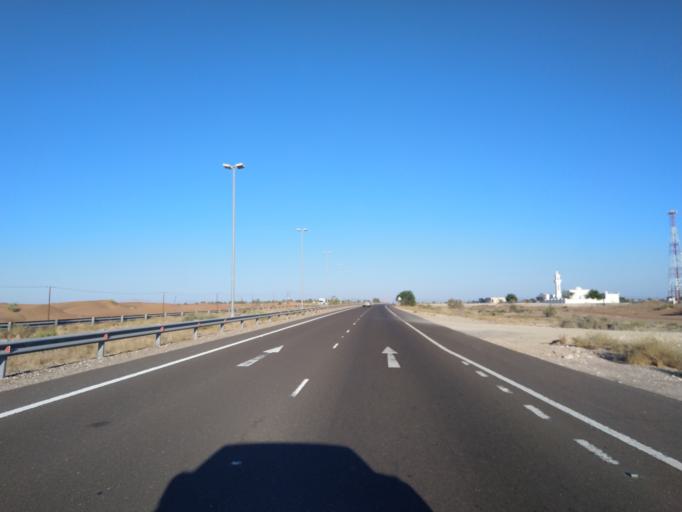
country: OM
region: Al Buraimi
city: Al Buraymi
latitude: 24.5402
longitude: 55.6312
